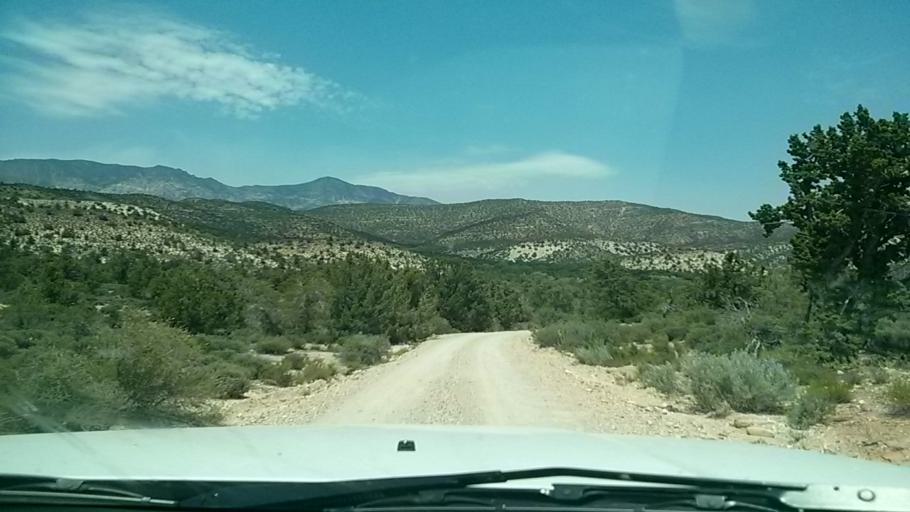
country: US
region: Utah
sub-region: Washington County
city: Washington
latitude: 37.2510
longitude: -113.4327
